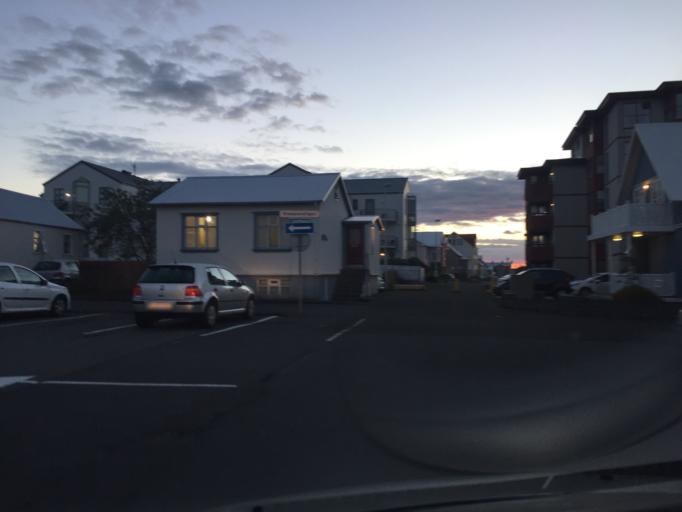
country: IS
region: Southern Peninsula
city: Reykjanesbaer
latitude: 64.0036
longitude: -22.5568
